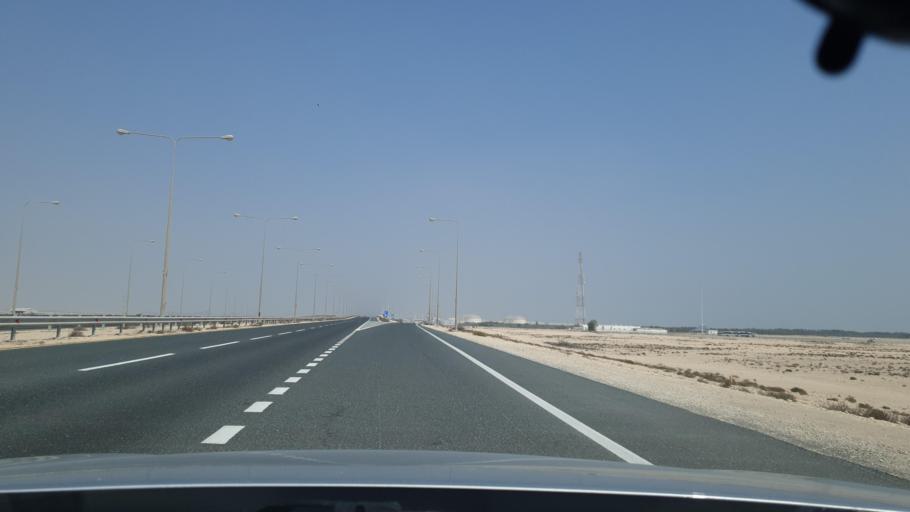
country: QA
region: Al Khawr
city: Al Khawr
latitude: 25.8360
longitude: 51.5265
